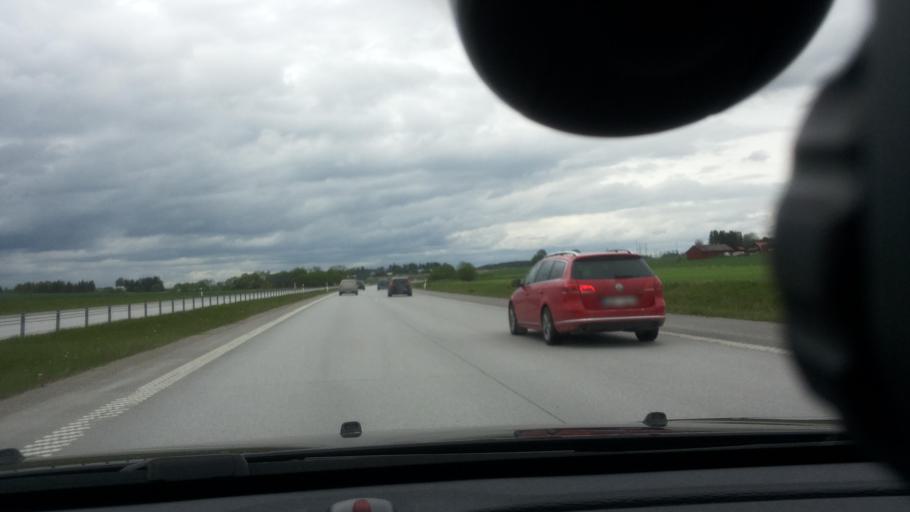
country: SE
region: Uppsala
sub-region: Uppsala Kommun
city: Gamla Uppsala
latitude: 59.8980
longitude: 17.6547
